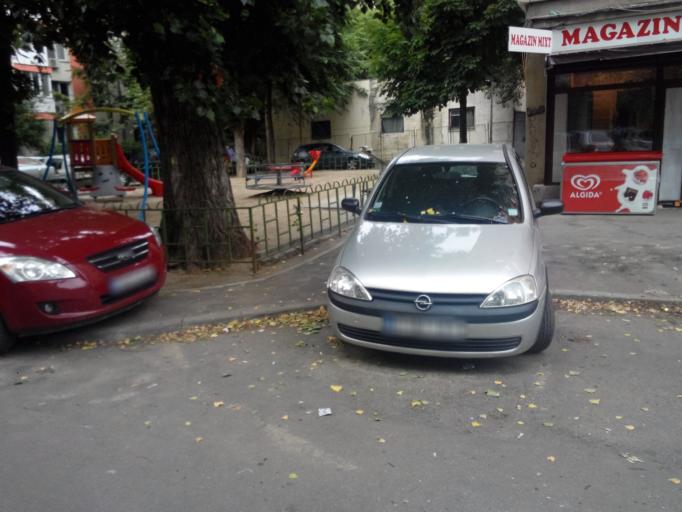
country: RO
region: Bucuresti
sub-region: Municipiul Bucuresti
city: Bucharest
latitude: 44.4464
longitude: 26.1214
